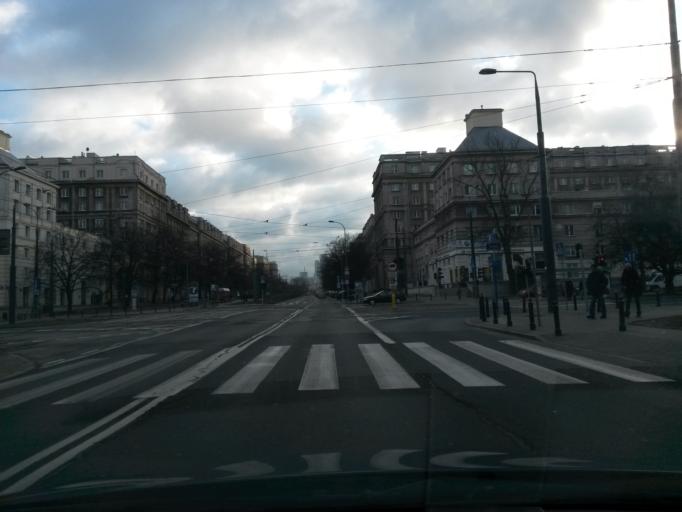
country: PL
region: Masovian Voivodeship
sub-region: Warszawa
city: Wola
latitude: 52.2541
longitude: 20.9976
